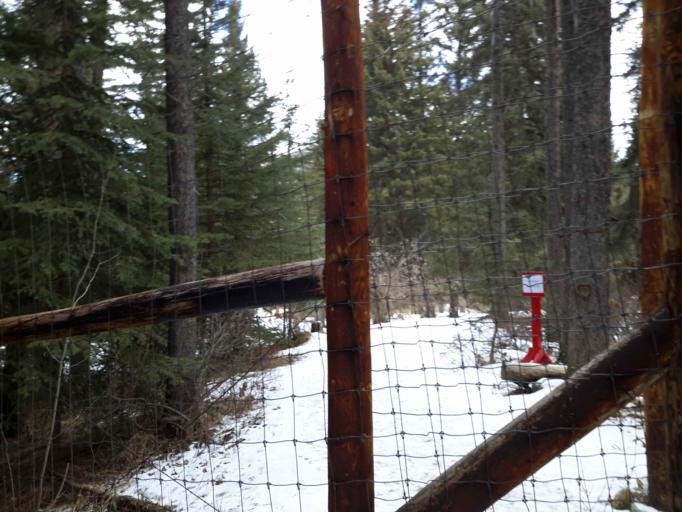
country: CA
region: Alberta
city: Banff
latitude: 51.1701
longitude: -115.5740
